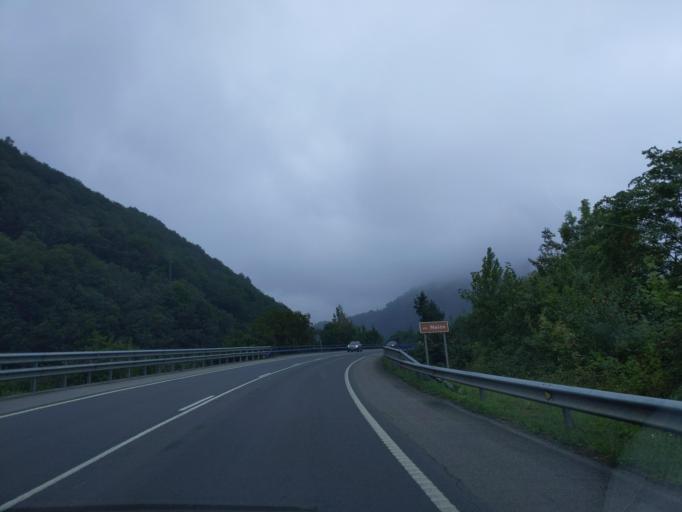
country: ES
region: Asturias
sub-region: Province of Asturias
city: Pola de Laviana
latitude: 43.2551
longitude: -5.5740
